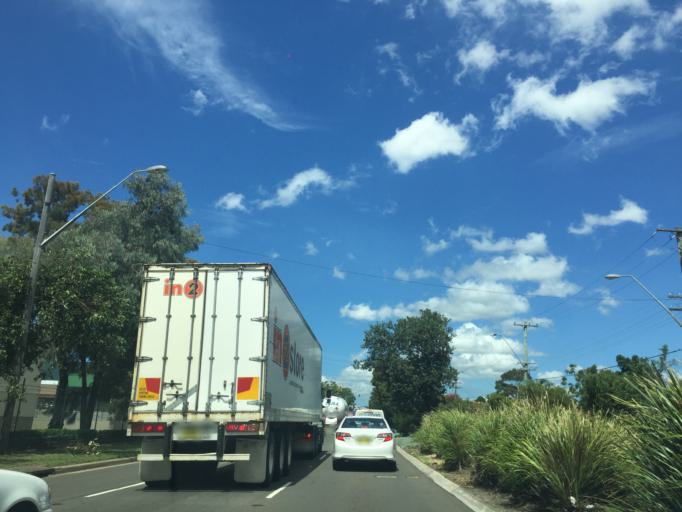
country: AU
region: New South Wales
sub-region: Strathfield
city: Strathfield South
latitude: -33.8988
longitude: 151.0655
